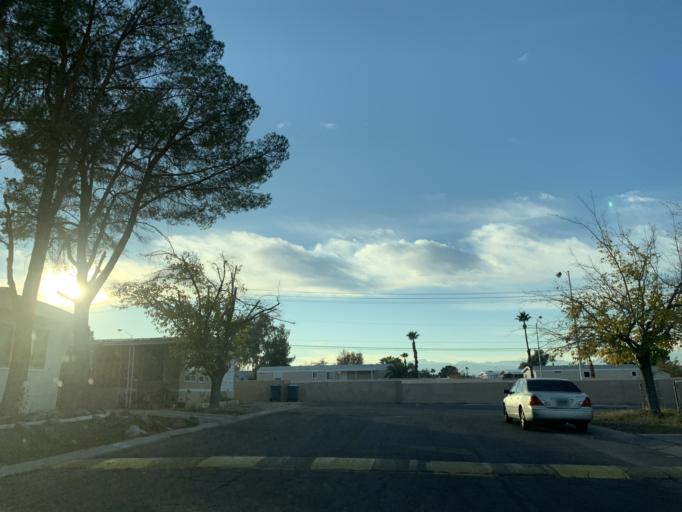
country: US
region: Nevada
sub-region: Clark County
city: Spring Valley
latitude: 36.1029
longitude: -115.2244
